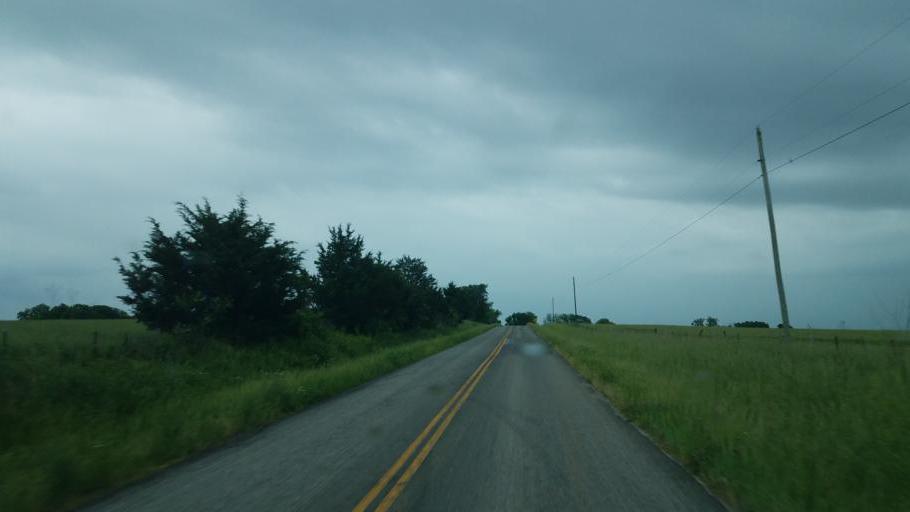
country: US
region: Missouri
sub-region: Moniteau County
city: California
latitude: 38.7633
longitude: -92.6053
